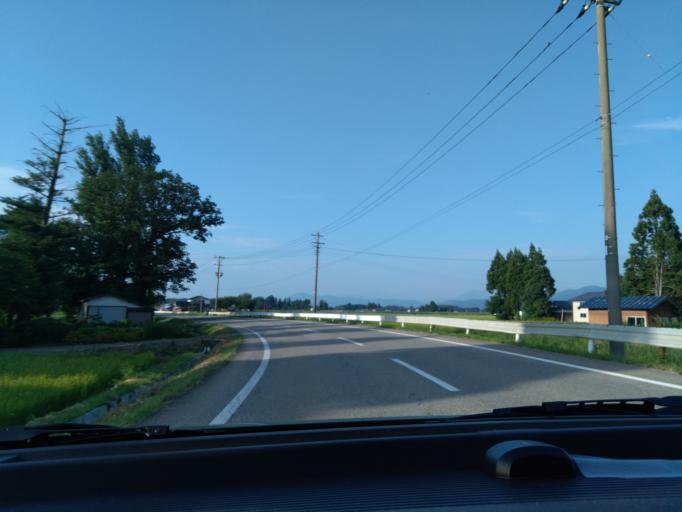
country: JP
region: Akita
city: Kakunodatemachi
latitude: 39.5280
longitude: 140.5584
